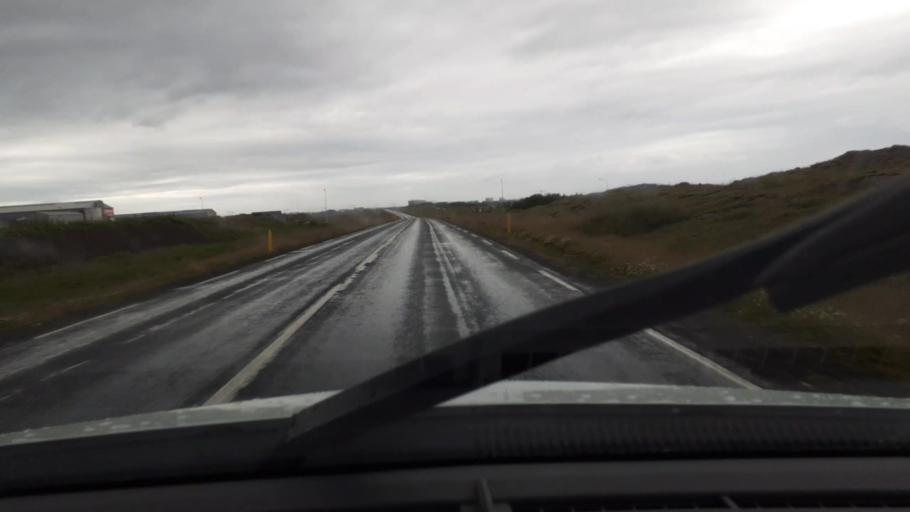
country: IS
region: West
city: Akranes
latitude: 64.3406
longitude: -22.0197
